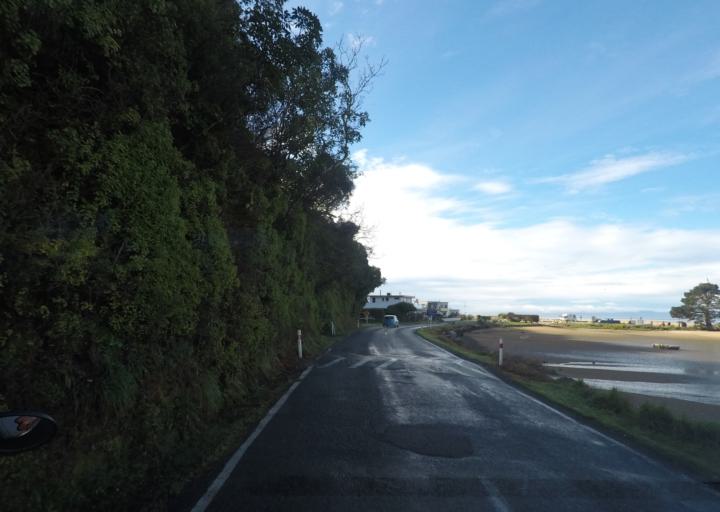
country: NZ
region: Tasman
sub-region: Tasman District
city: Motueka
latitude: -41.0090
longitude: 173.0062
